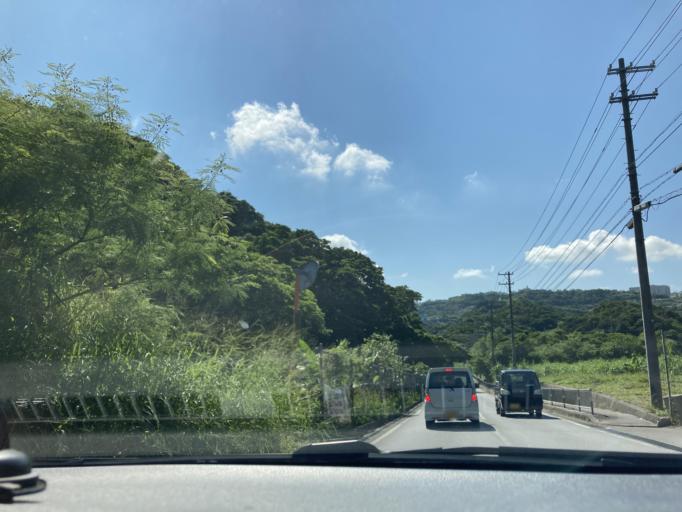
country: JP
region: Okinawa
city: Ginowan
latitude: 26.2226
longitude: 127.7473
